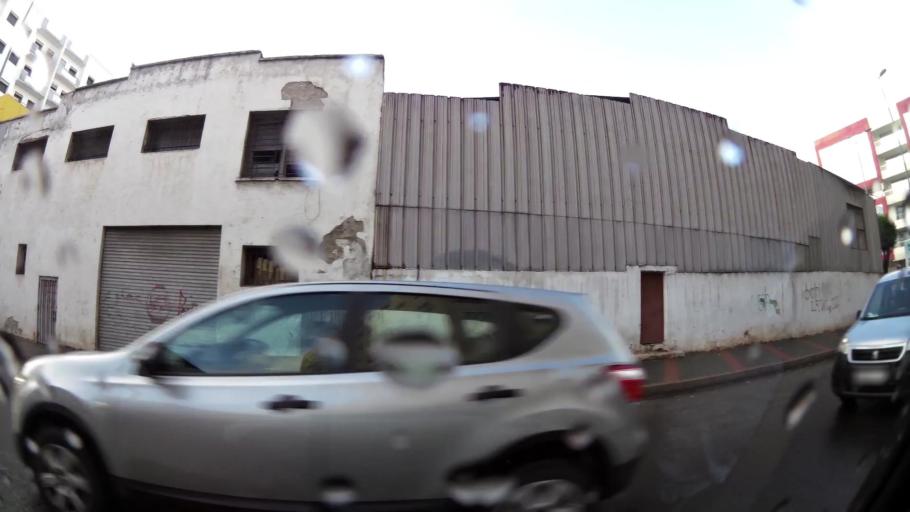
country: MA
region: Grand Casablanca
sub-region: Casablanca
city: Casablanca
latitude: 33.5873
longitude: -7.6003
